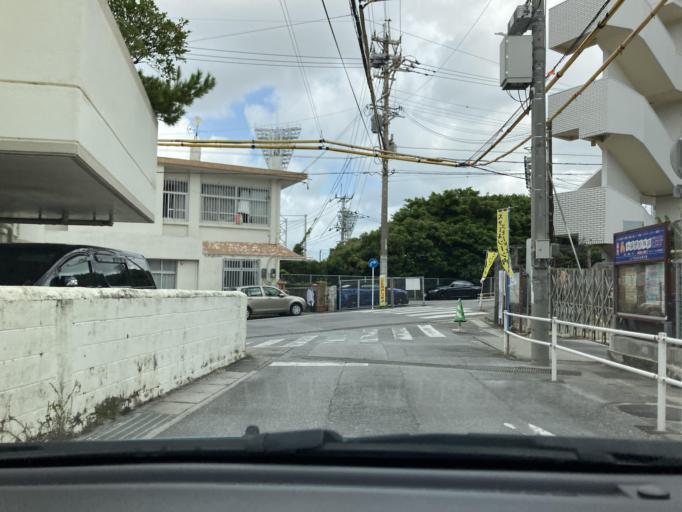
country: JP
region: Okinawa
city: Naha-shi
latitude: 26.2026
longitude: 127.6711
